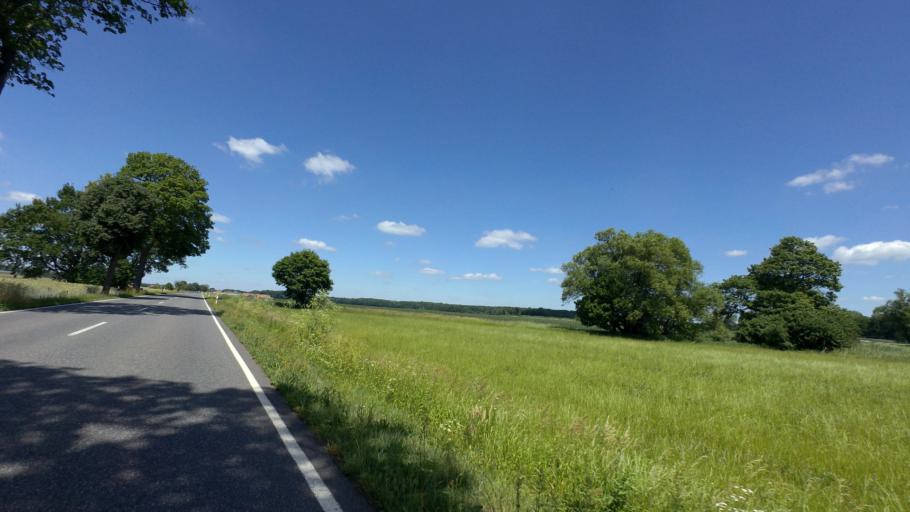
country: DE
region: Brandenburg
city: Kasel-Golzig
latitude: 51.9374
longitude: 13.6601
